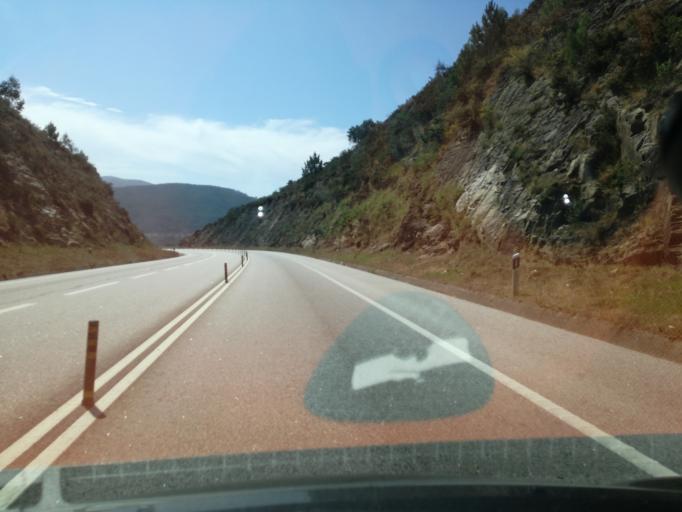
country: PT
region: Viana do Castelo
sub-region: Vila Nova de Cerveira
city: Vila Nova de Cerveira
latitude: 41.8993
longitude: -8.7869
